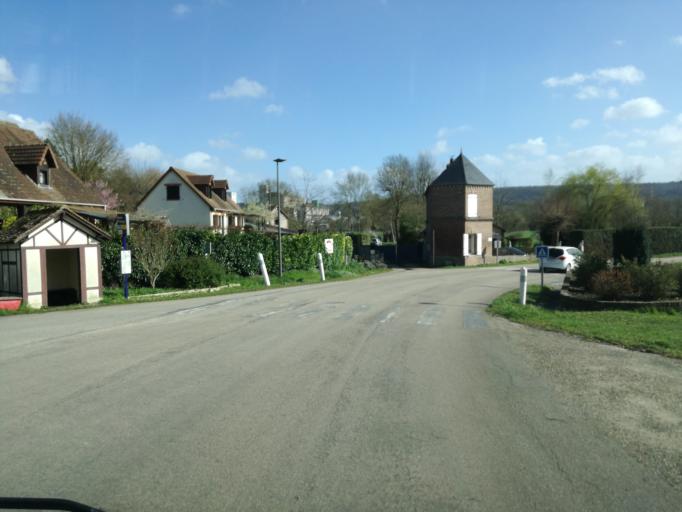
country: FR
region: Haute-Normandie
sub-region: Departement de la Seine-Maritime
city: Grand-Couronne
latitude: 49.3615
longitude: 0.9789
